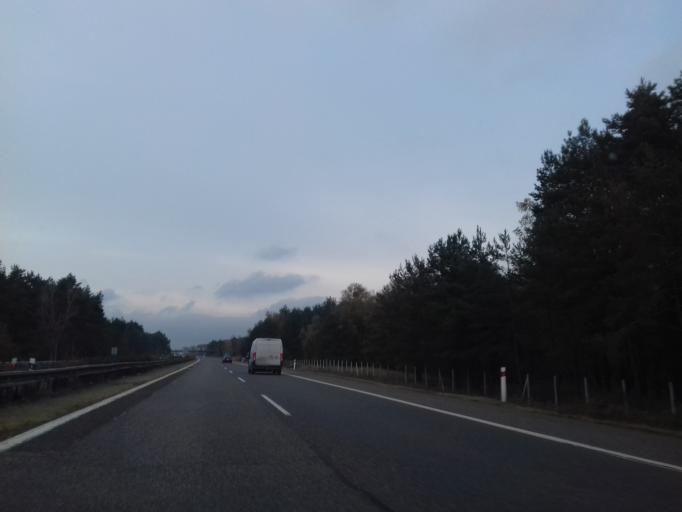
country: CZ
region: South Moravian
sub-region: Okres Breclav
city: Lanzhot
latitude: 48.6237
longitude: 17.0099
